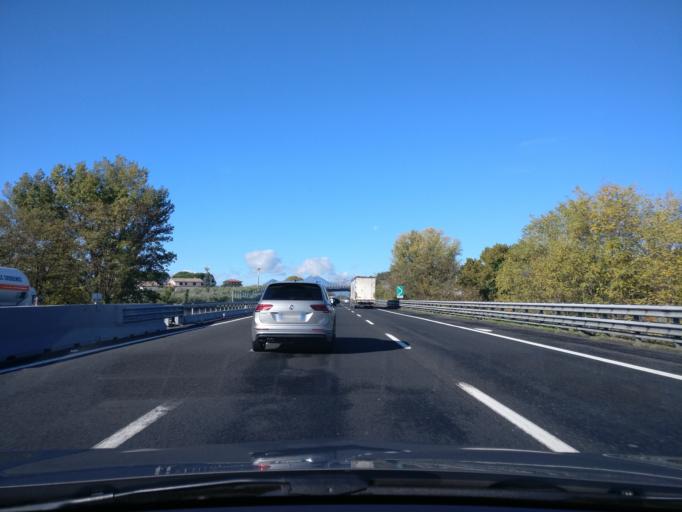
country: IT
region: Latium
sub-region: Provincia di Frosinone
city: Pofi
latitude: 41.5565
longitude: 13.4214
